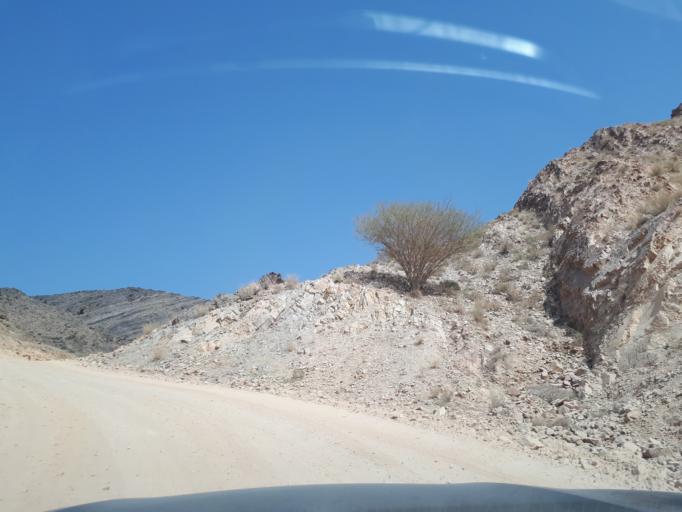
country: OM
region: Ash Sharqiyah
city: Al Qabil
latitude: 23.0558
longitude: 58.9640
